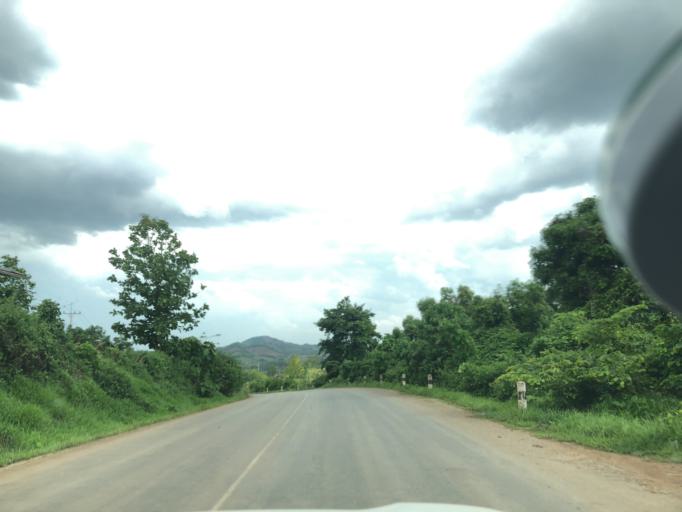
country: TH
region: Uttaradit
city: Ban Khok
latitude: 18.1236
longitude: 101.3721
